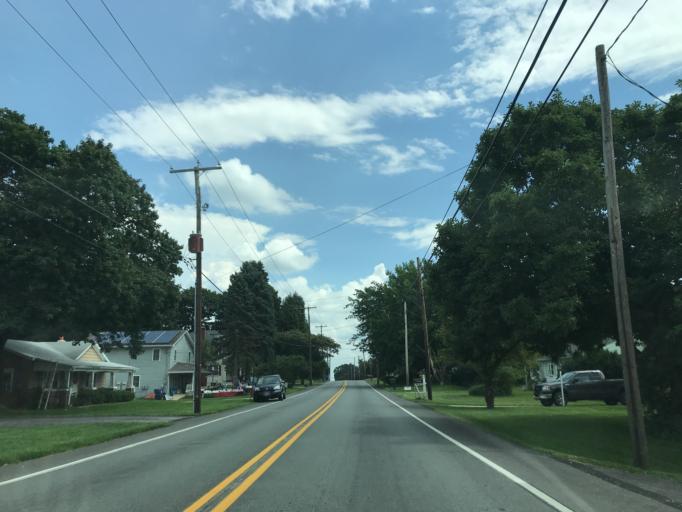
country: US
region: Pennsylvania
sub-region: York County
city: Windsor
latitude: 39.8892
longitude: -76.5528
